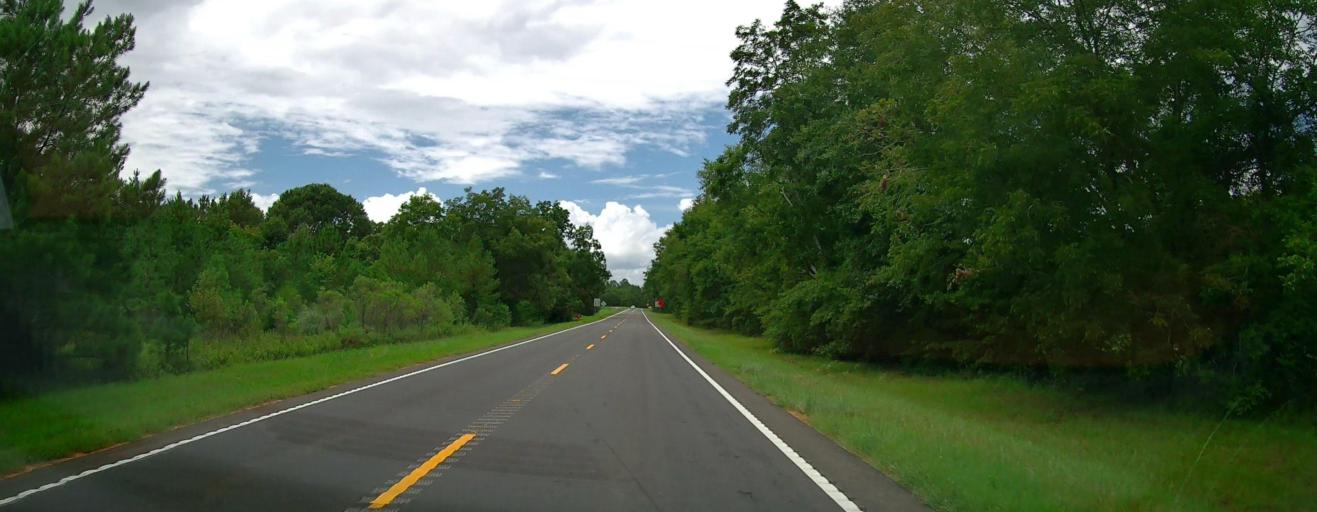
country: US
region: Georgia
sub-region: Wilcox County
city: Rochelle
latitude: 32.0932
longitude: -83.5883
